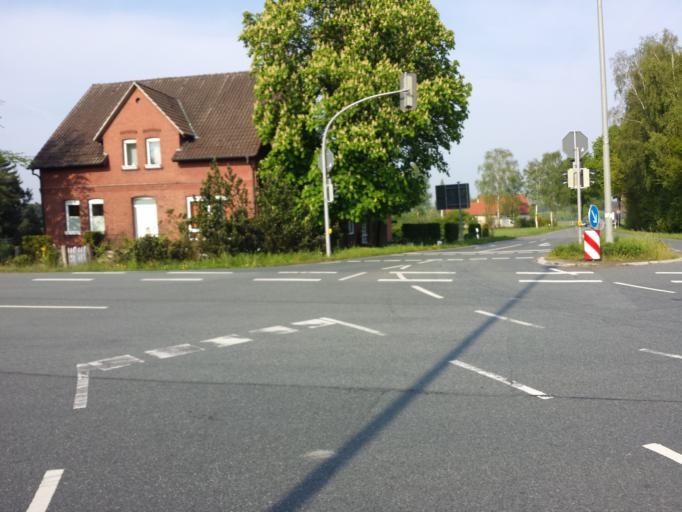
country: DE
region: North Rhine-Westphalia
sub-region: Regierungsbezirk Detmold
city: Guetersloh
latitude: 51.9521
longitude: 8.3437
